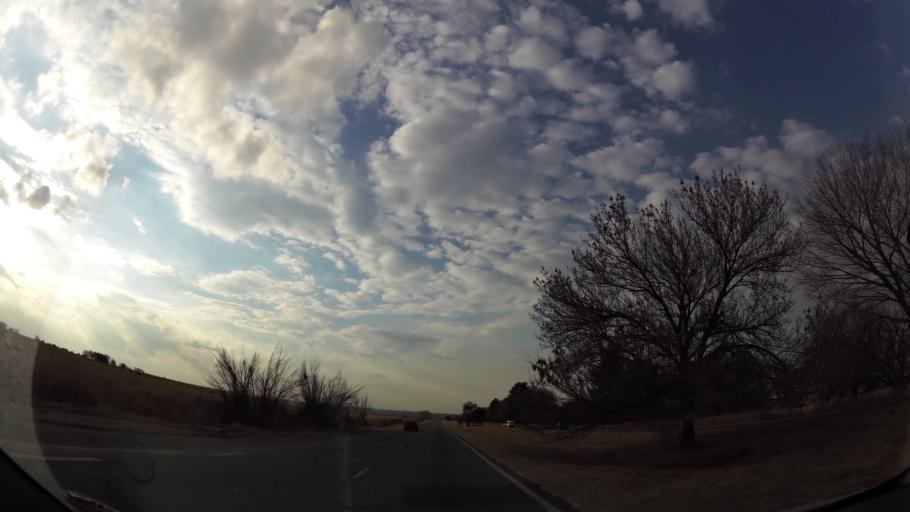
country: ZA
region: Orange Free State
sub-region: Fezile Dabi District Municipality
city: Sasolburg
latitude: -26.7749
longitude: 27.8246
